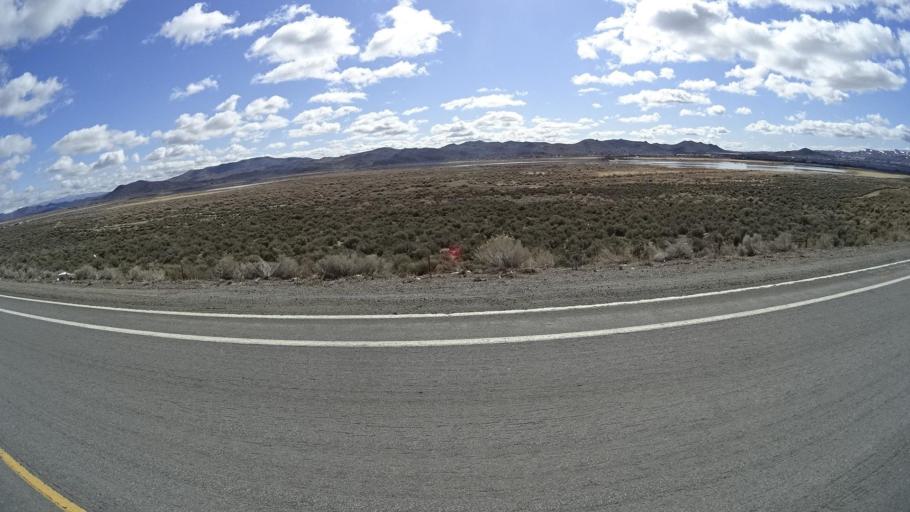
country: US
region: Nevada
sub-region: Washoe County
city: Lemmon Valley
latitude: 39.6605
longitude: -119.8632
